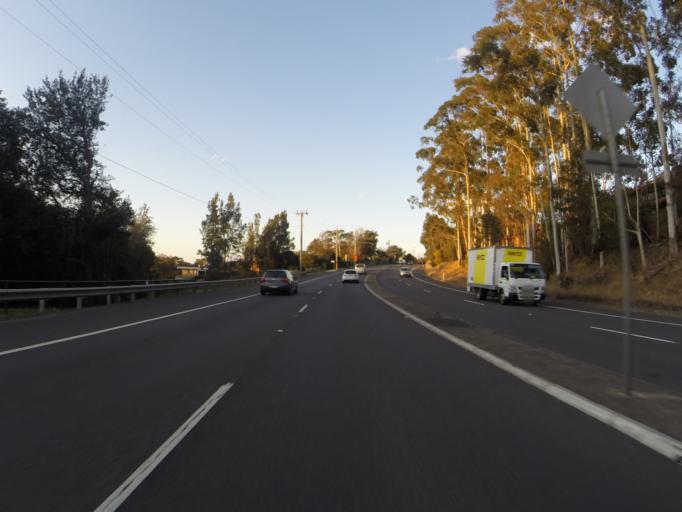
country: AU
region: New South Wales
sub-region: Blue Mountains Municipality
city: Blaxland
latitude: -33.6993
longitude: 150.5616
